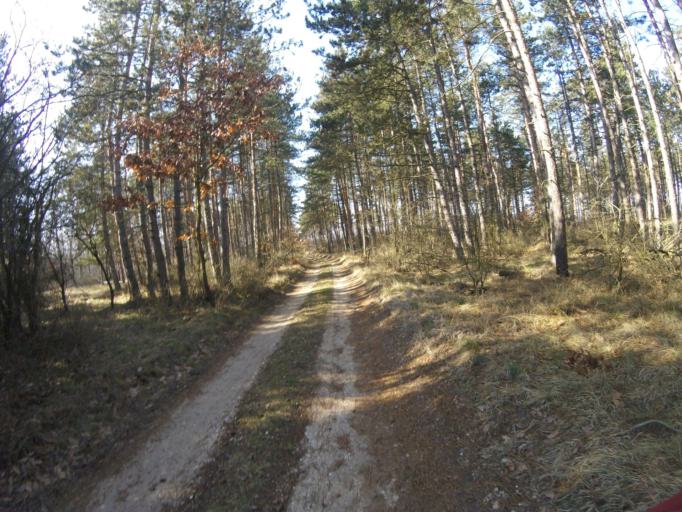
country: HU
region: Komarom-Esztergom
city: Oroszlany
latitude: 47.4615
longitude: 18.3533
